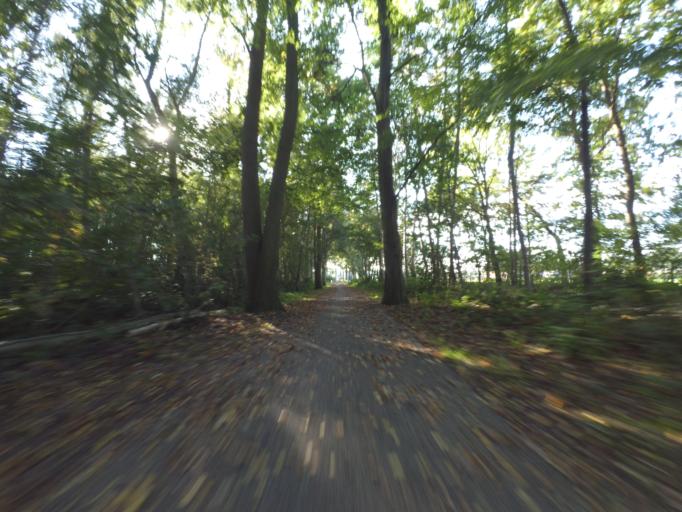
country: NL
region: Gelderland
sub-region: Gemeente Nijkerk
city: Nijkerk
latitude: 52.2246
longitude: 5.5267
